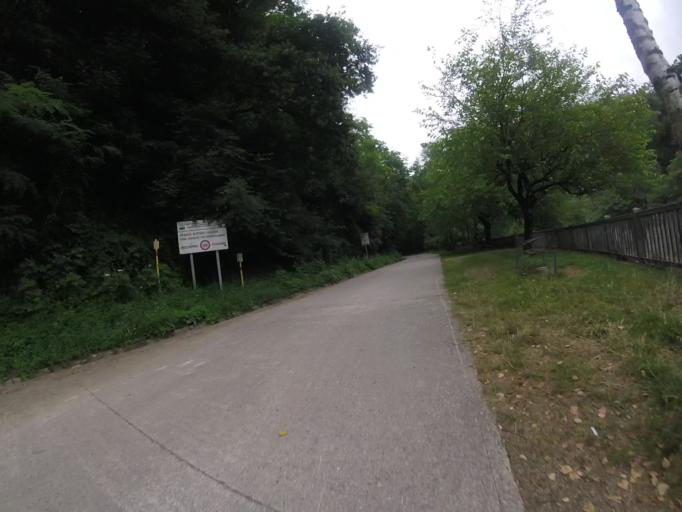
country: ES
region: Navarre
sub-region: Provincia de Navarra
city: Doneztebe
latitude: 43.1353
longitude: -1.6659
